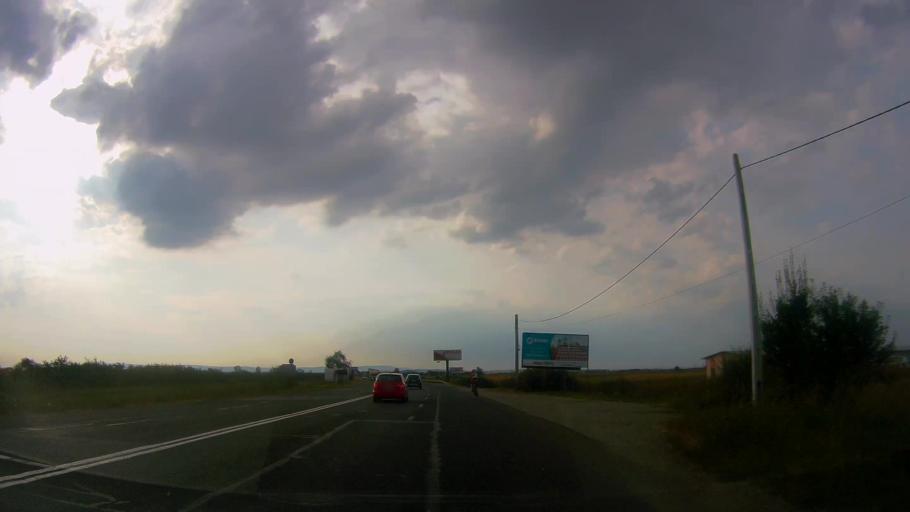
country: RO
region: Satu Mare
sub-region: Oras Ardud
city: Madaras
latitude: 47.7286
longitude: 22.8830
